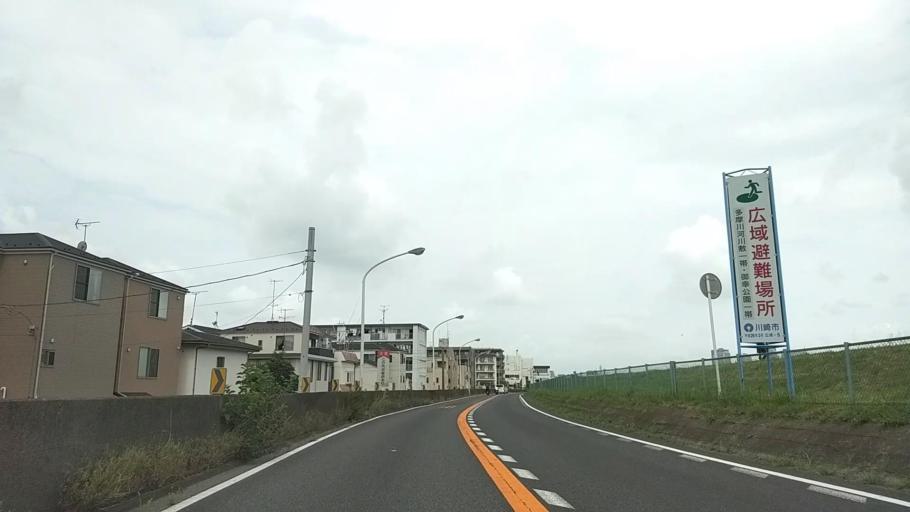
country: JP
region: Kanagawa
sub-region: Kawasaki-shi
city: Kawasaki
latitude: 35.5542
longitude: 139.6899
